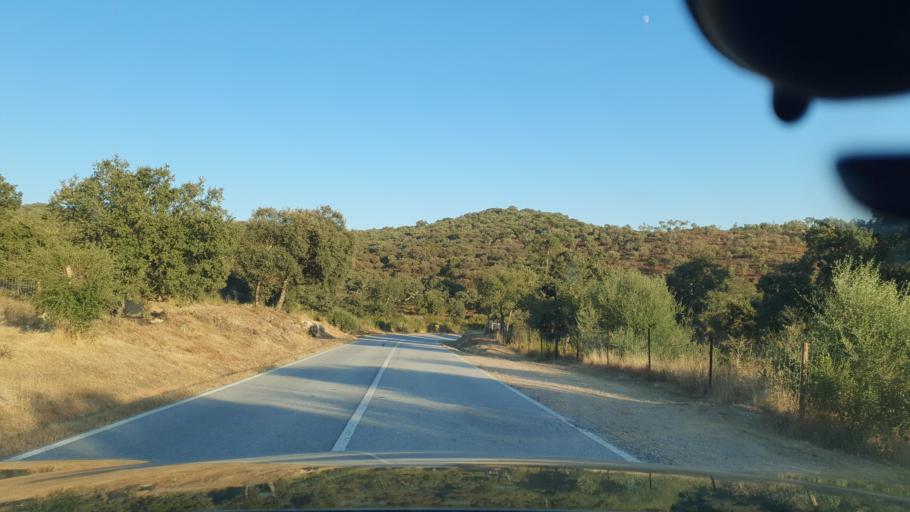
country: PT
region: Evora
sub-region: Estremoz
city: Estremoz
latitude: 38.9109
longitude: -7.6628
